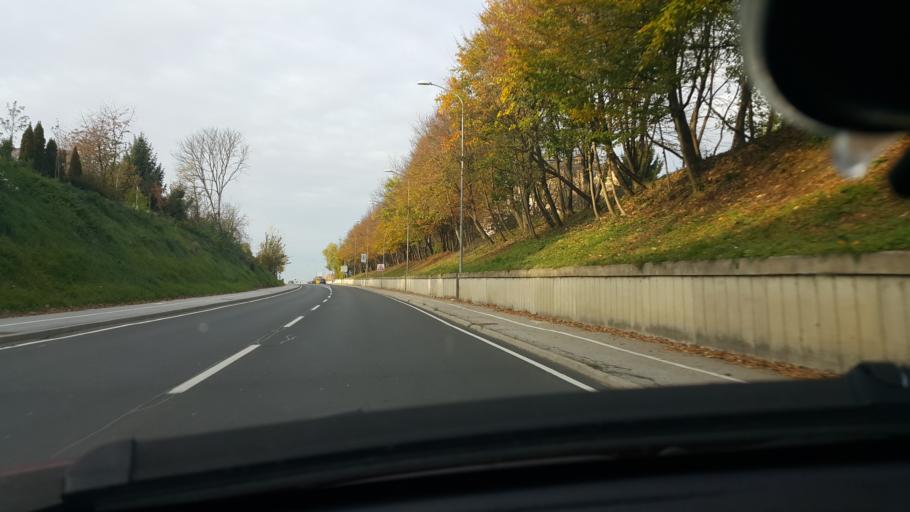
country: SI
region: Brezice
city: Brezice
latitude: 45.9027
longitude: 15.6040
